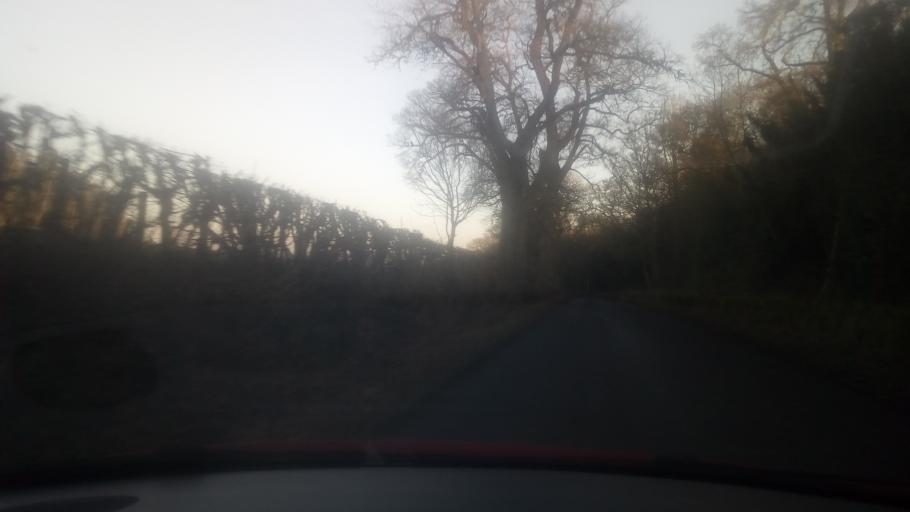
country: GB
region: Scotland
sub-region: The Scottish Borders
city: Jedburgh
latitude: 55.5179
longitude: -2.5564
